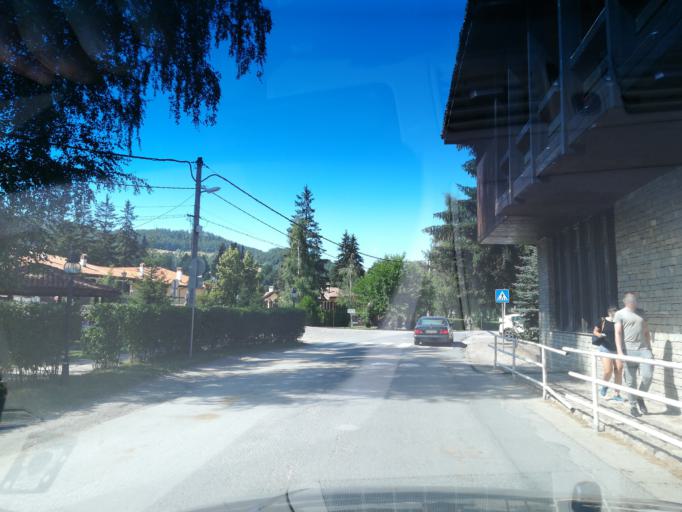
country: BG
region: Sofiya
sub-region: Obshtina Koprivshtitsa
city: Koprivshtitsa
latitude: 42.6369
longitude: 24.3600
